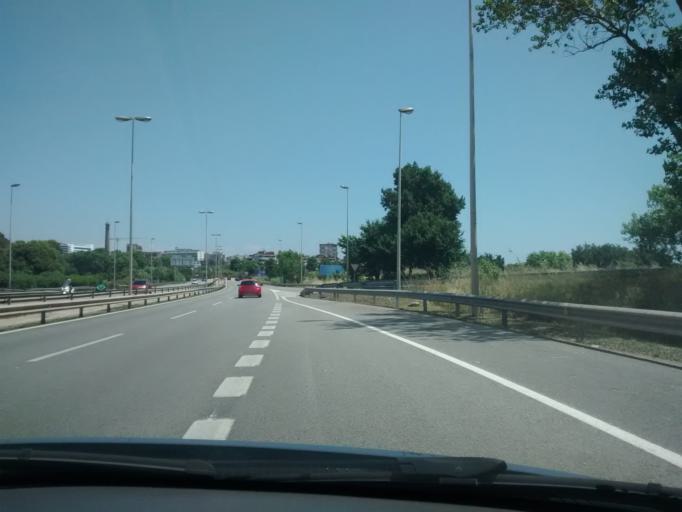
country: ES
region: Catalonia
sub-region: Provincia de Barcelona
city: Sant Joan Despi
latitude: 41.3532
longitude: 2.0589
